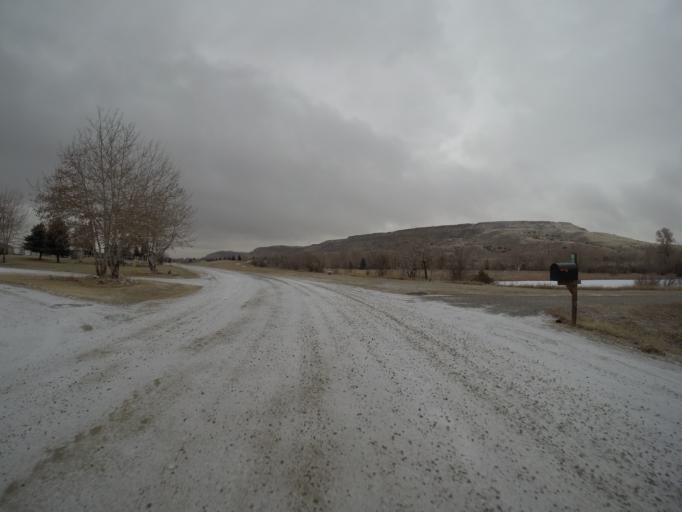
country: US
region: Montana
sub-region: Stillwater County
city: Absarokee
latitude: 45.5330
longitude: -109.4425
